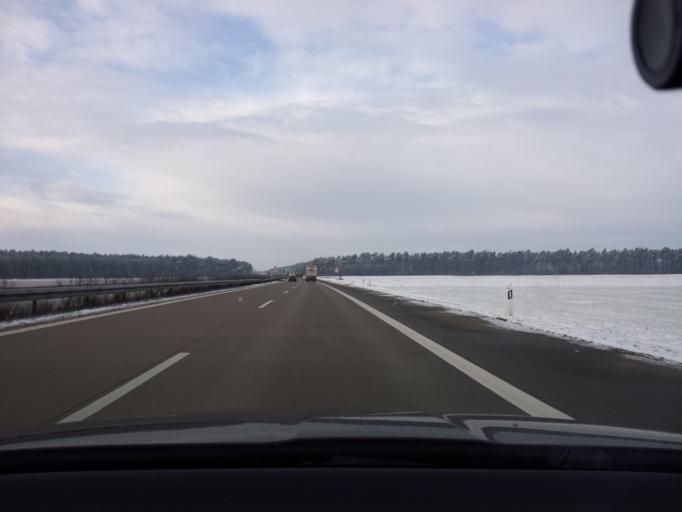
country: DE
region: Mecklenburg-Vorpommern
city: Rastow
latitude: 53.4321
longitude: 11.4723
